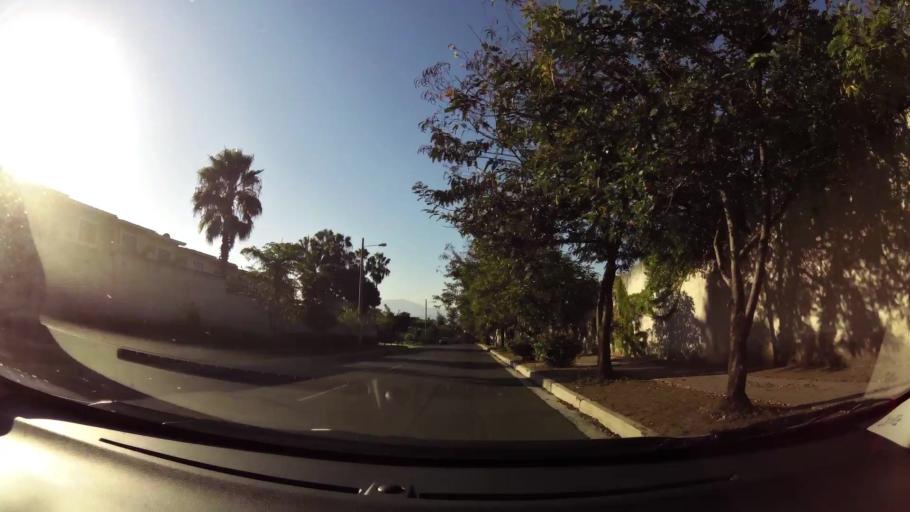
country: SV
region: La Libertad
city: Santa Tecla
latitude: 13.7397
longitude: -89.3552
